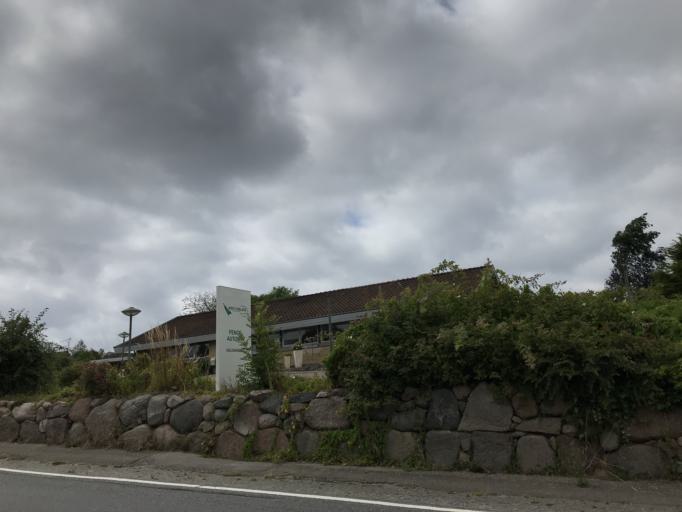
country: DK
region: South Denmark
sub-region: Faaborg-Midtfyn Kommune
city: Faaborg
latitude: 54.9395
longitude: 10.2581
